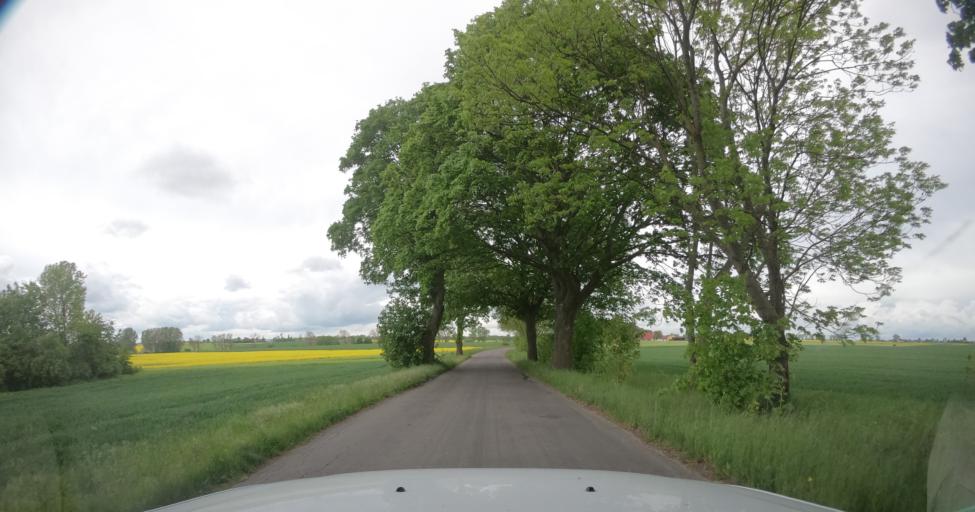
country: PL
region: West Pomeranian Voivodeship
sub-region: Powiat pyrzycki
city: Lipiany
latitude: 53.0655
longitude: 14.9282
